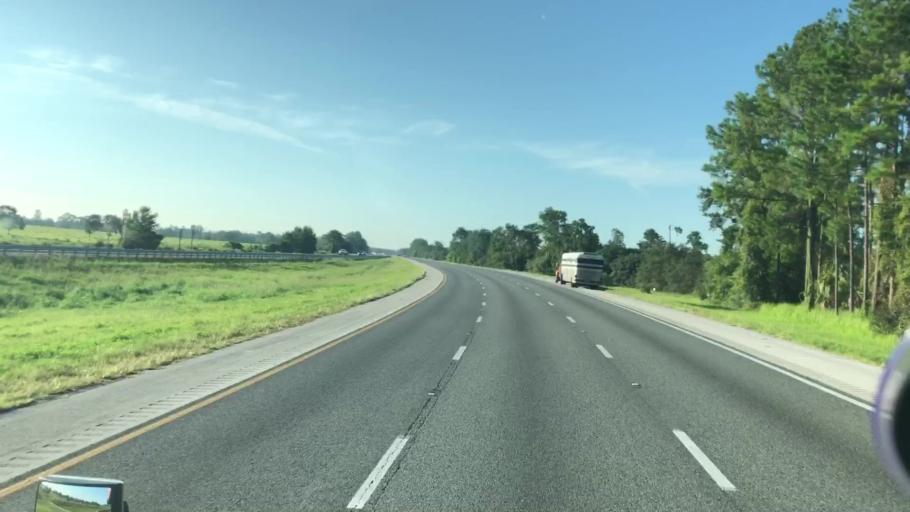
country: US
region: Florida
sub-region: Marion County
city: Ocala
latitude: 29.0772
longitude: -82.1846
